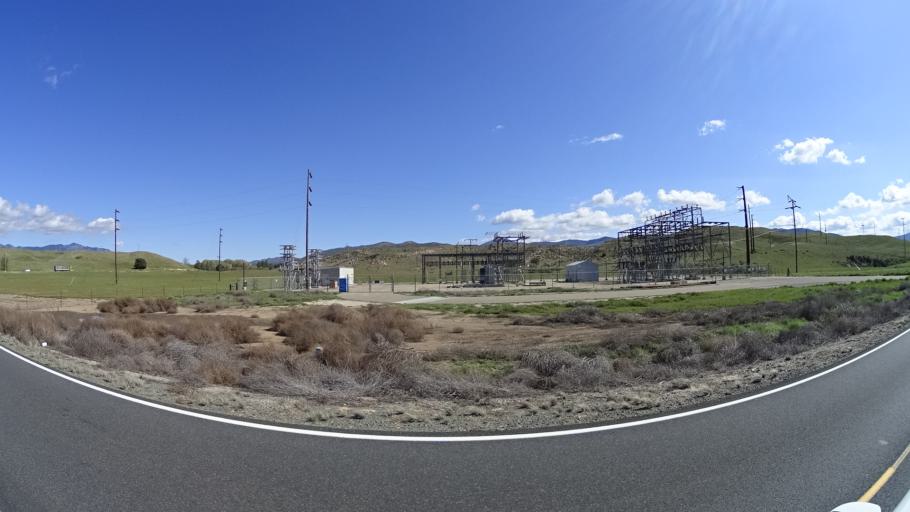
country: US
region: California
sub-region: San Diego County
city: Julian
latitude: 33.2481
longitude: -116.6762
